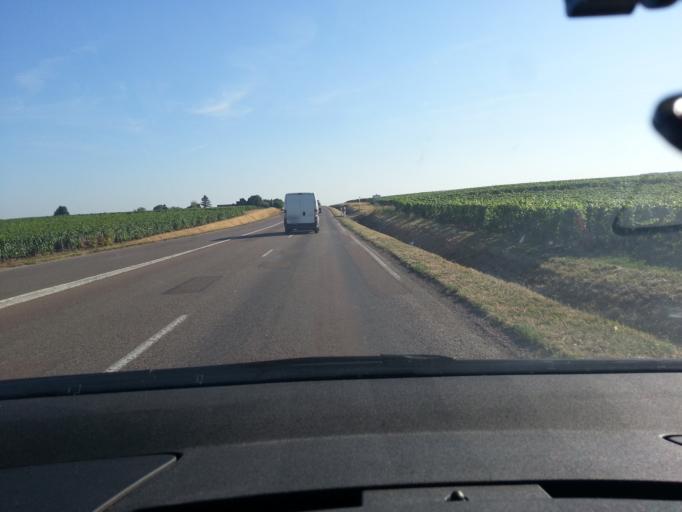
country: FR
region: Bourgogne
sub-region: Departement de la Cote-d'Or
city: Beaune
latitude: 47.0567
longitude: 4.8597
